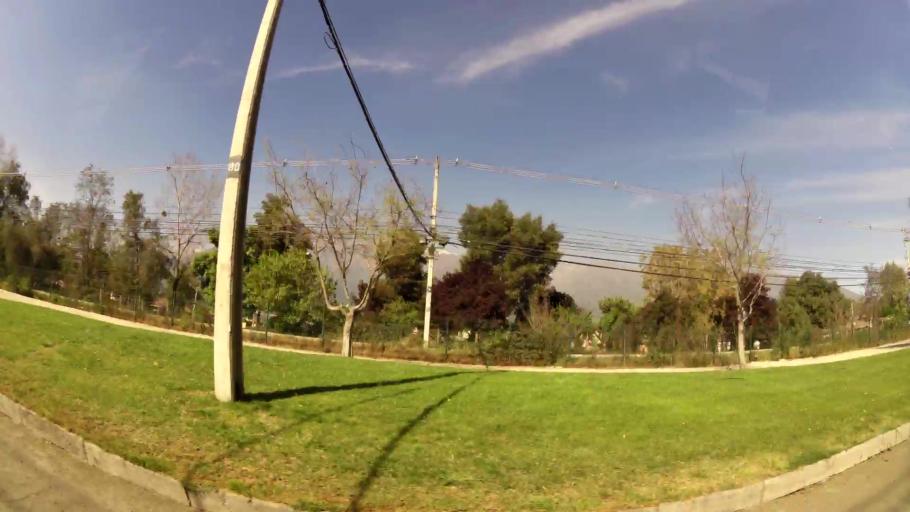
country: CL
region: Santiago Metropolitan
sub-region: Provincia de Santiago
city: Villa Presidente Frei, Nunoa, Santiago, Chile
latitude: -33.4814
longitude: -70.5581
